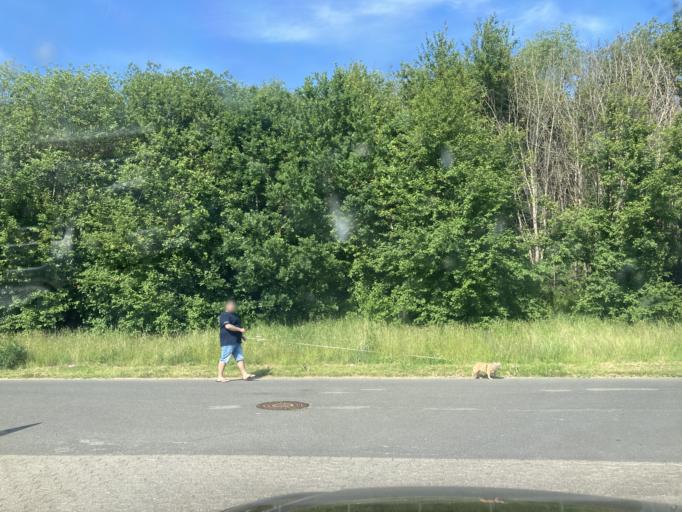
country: DK
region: Capital Region
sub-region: Hillerod Kommune
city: Nodebo
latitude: 55.9421
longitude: 12.3492
